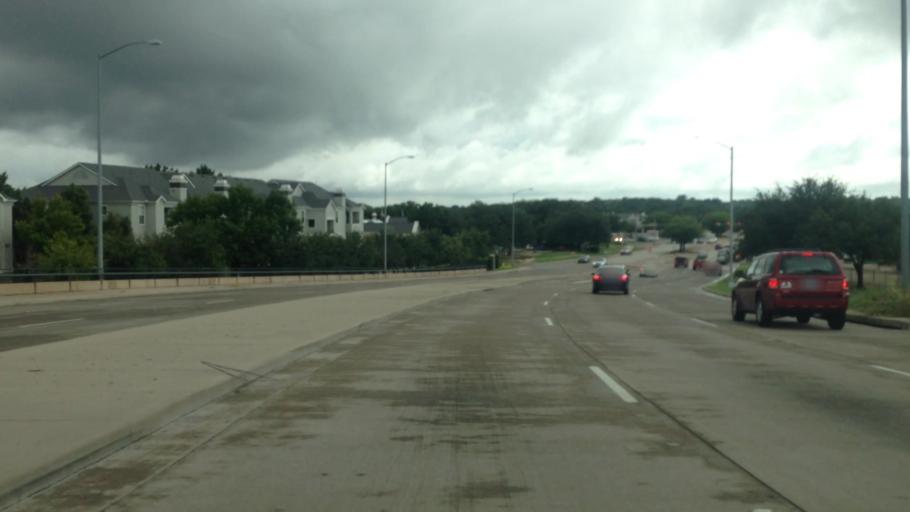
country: US
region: Texas
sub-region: Tarrant County
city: Westworth
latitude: 32.7154
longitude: -97.3849
